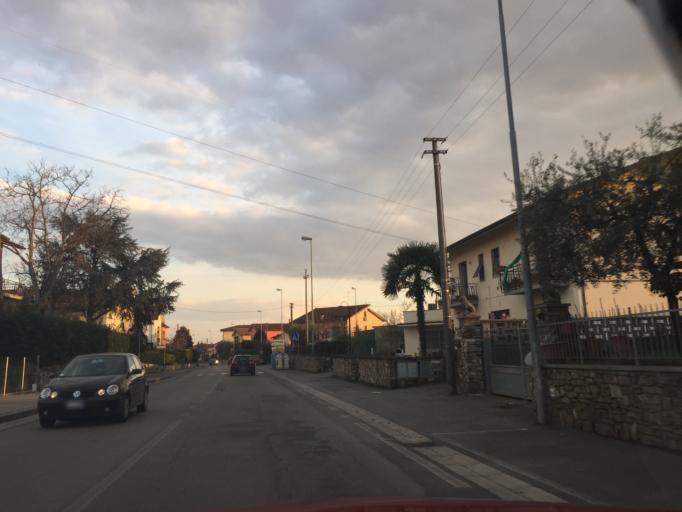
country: IT
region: Tuscany
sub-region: Provincia di Pistoia
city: Borgo a Buggiano
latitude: 43.8706
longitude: 10.7366
